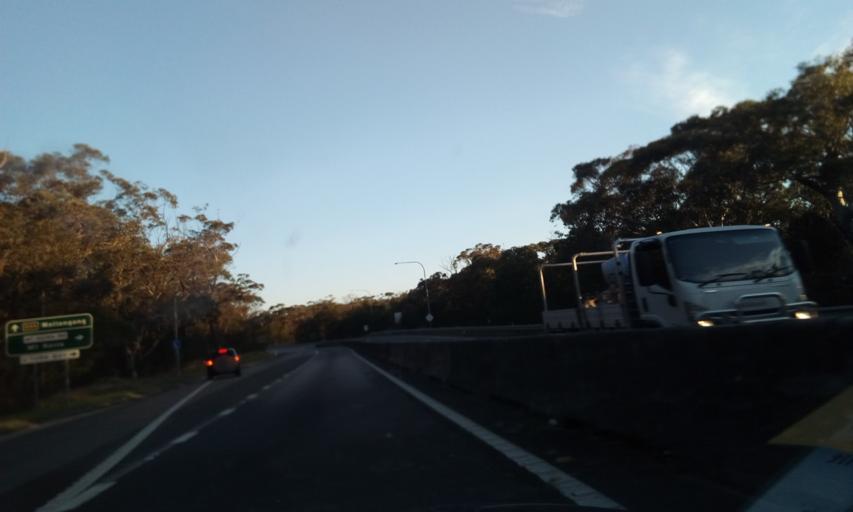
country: AU
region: New South Wales
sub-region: Wollongong
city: Mount Keira
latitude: -34.3728
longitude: 150.8300
